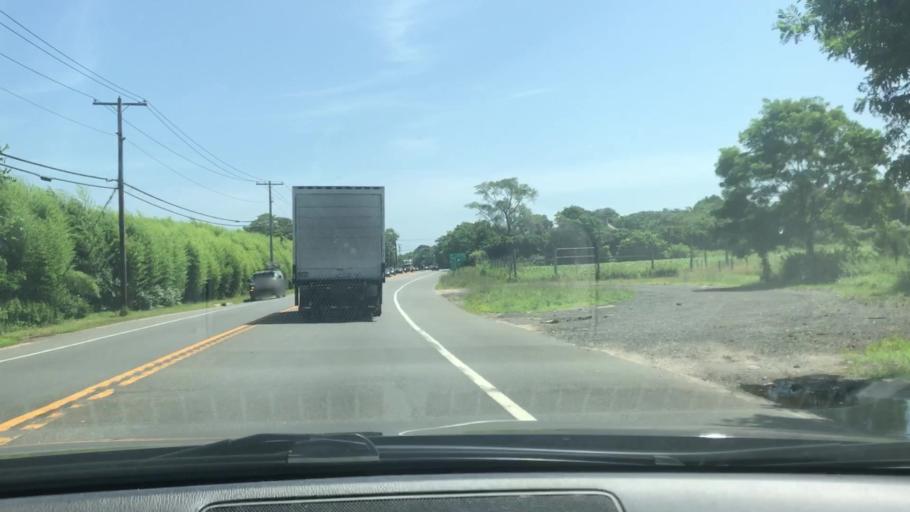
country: US
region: New York
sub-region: Suffolk County
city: Bridgehampton
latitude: 40.9410
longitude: -72.2825
